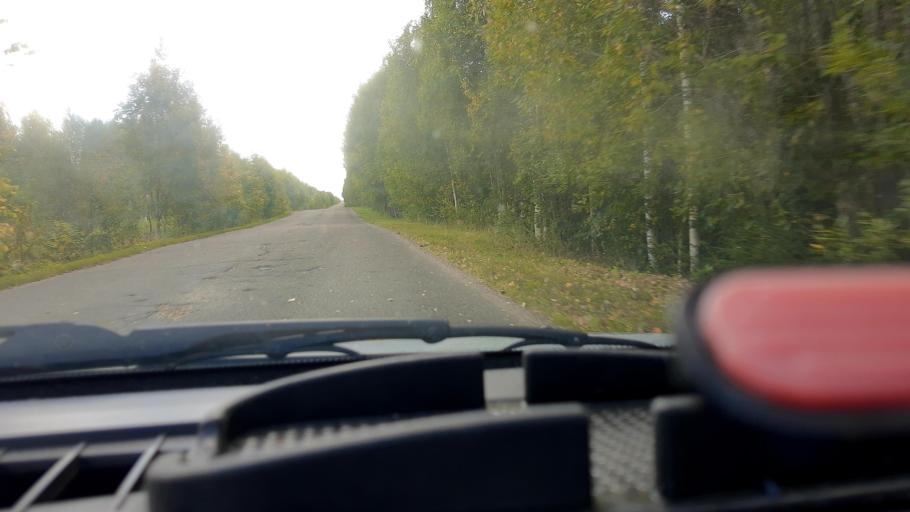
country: RU
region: Mariy-El
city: Kilemary
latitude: 56.9080
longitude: 46.7329
